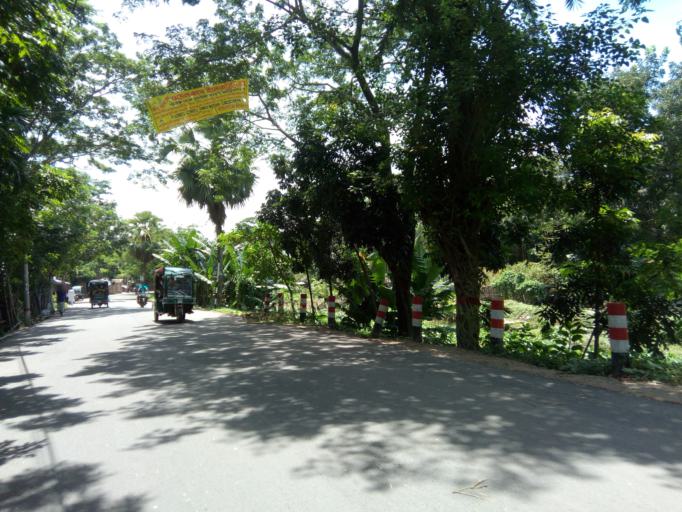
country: BD
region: Dhaka
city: Tungipara
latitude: 22.8972
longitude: 89.8909
